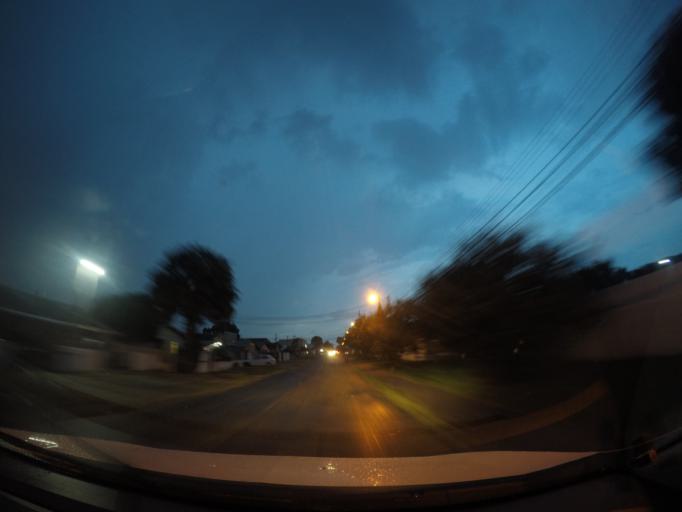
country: BR
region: Parana
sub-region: Sao Jose Dos Pinhais
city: Sao Jose dos Pinhais
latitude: -25.5105
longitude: -49.2291
